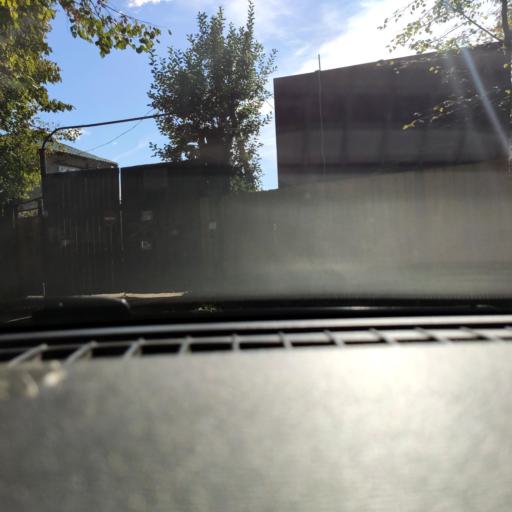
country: RU
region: Perm
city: Perm
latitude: 58.0747
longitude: 56.3726
